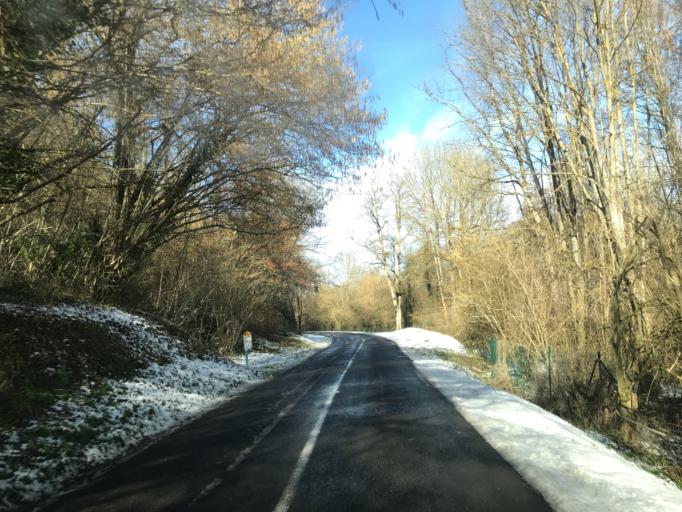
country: FR
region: Haute-Normandie
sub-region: Departement de l'Eure
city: Houlbec-Cocherel
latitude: 49.0769
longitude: 1.2816
